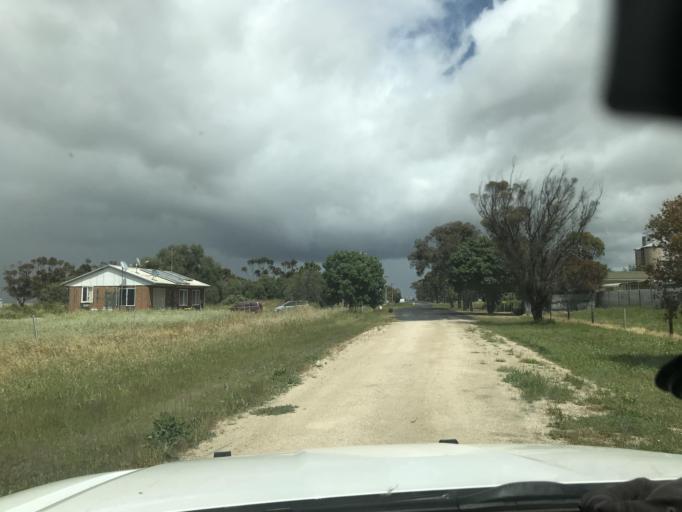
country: AU
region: South Australia
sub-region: Tatiara
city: Bordertown
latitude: -36.3764
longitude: 140.9913
